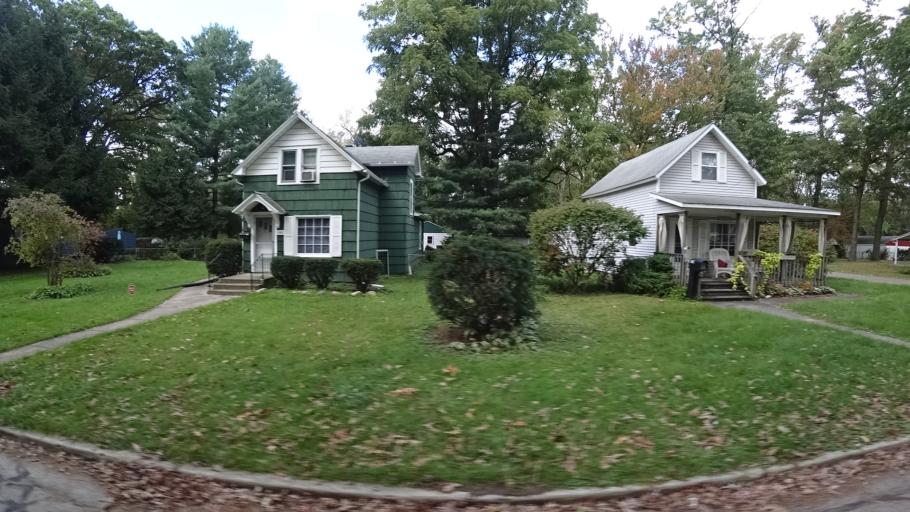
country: US
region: Indiana
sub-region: LaPorte County
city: Trail Creek
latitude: 41.7032
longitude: -86.8758
